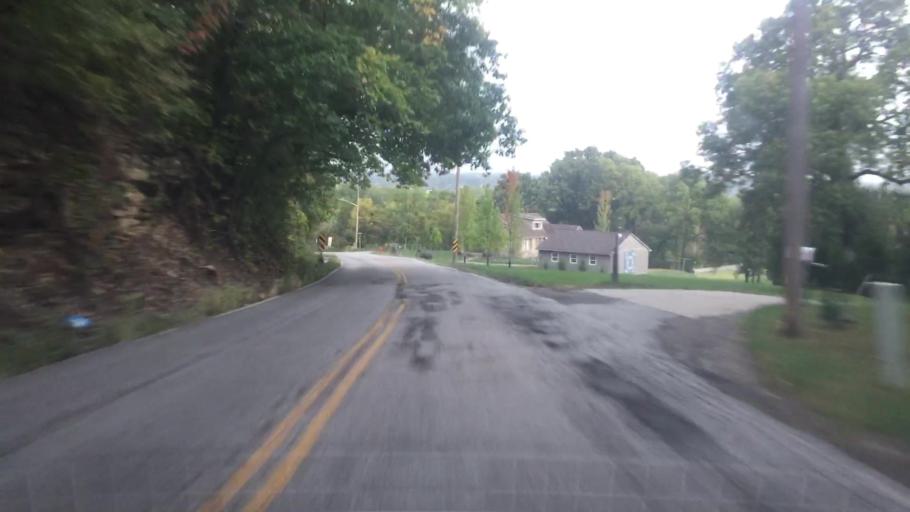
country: US
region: Kansas
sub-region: Johnson County
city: Shawnee
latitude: 39.0462
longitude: -94.7599
